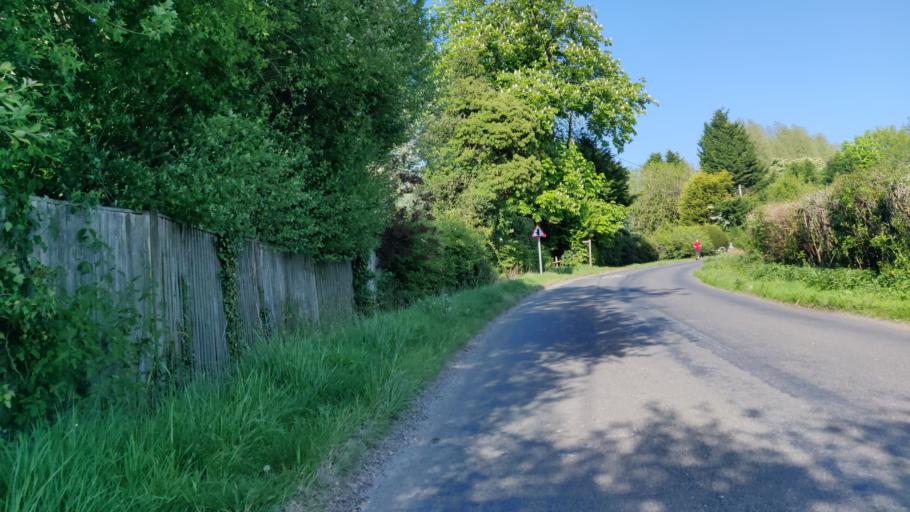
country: GB
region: England
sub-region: West Sussex
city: Southwater
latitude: 51.0327
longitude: -0.3680
